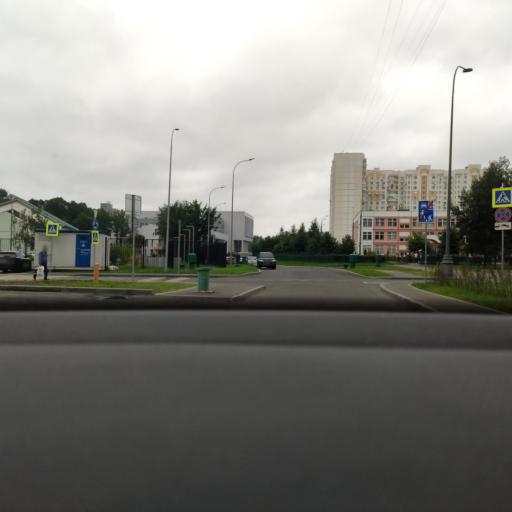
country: RU
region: Moscow
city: Severnyy
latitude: 55.9356
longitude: 37.5541
